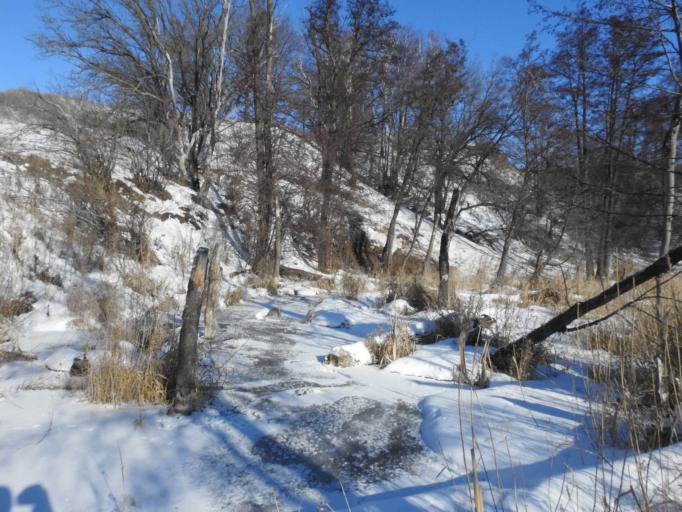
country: RU
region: Saratov
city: Lysyye Gory
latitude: 51.4643
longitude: 44.9680
